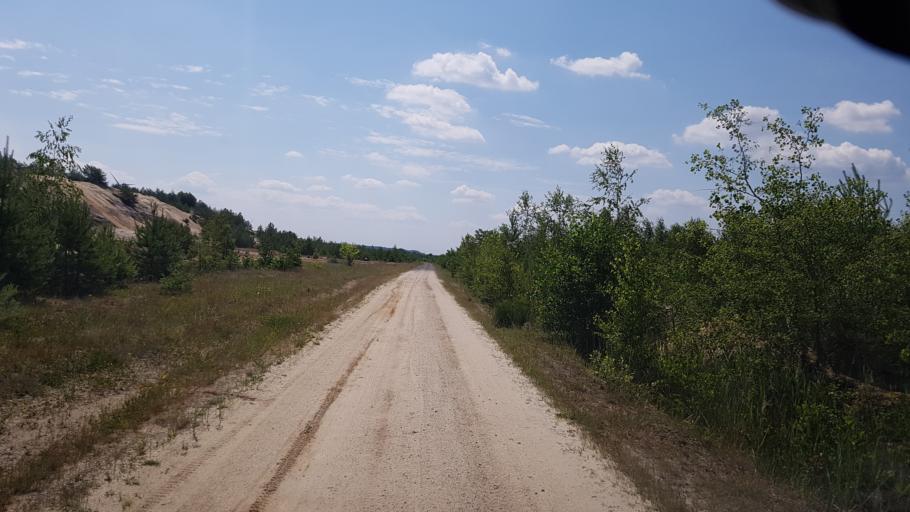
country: DE
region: Brandenburg
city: Sallgast
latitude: 51.5697
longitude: 13.8047
